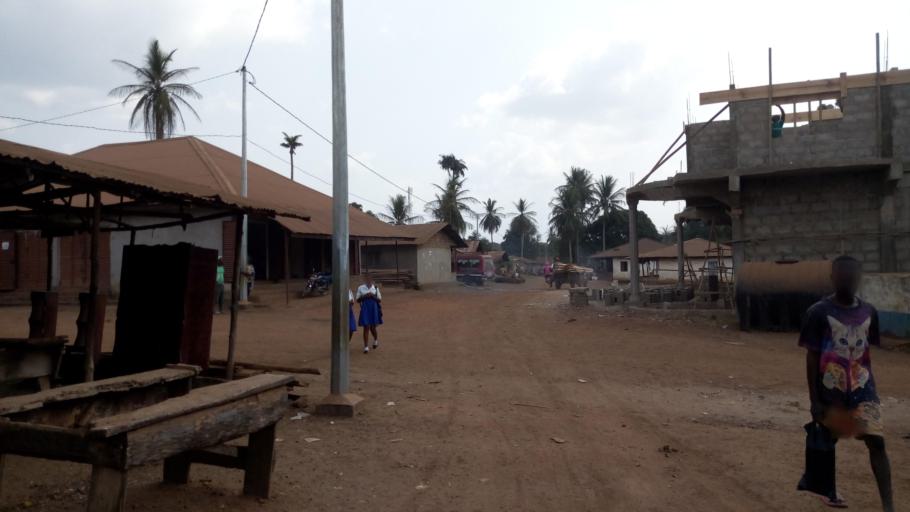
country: SL
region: Southern Province
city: Mogbwemo
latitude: 7.7873
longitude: -12.2982
